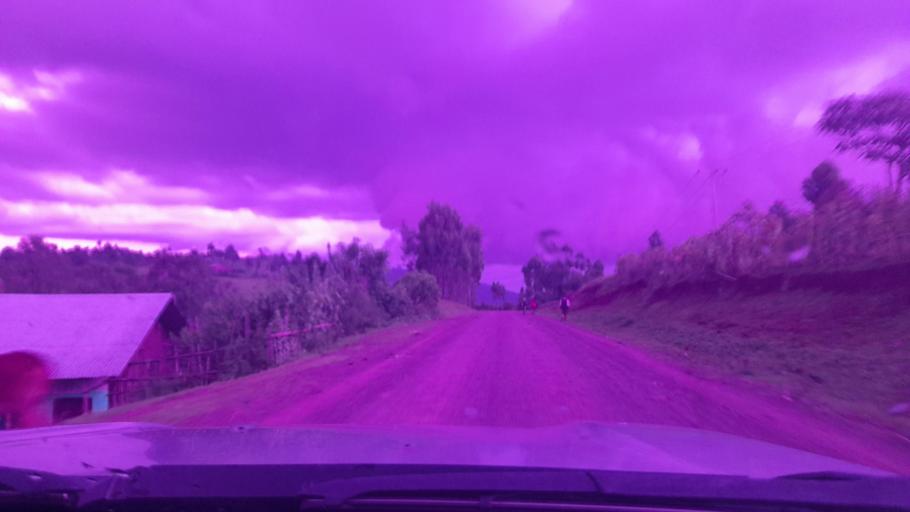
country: ET
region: Southern Nations, Nationalities, and People's Region
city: Mizan Teferi
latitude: 6.9056
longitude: 35.8419
